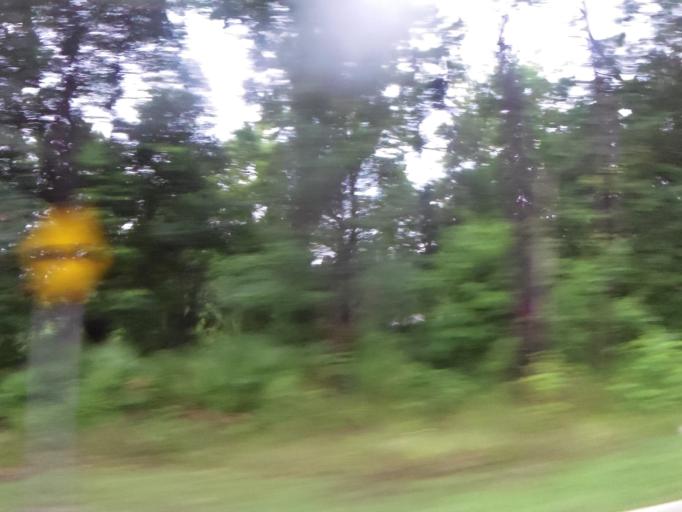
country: US
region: Florida
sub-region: Duval County
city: Jacksonville
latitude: 30.2761
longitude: -81.5626
